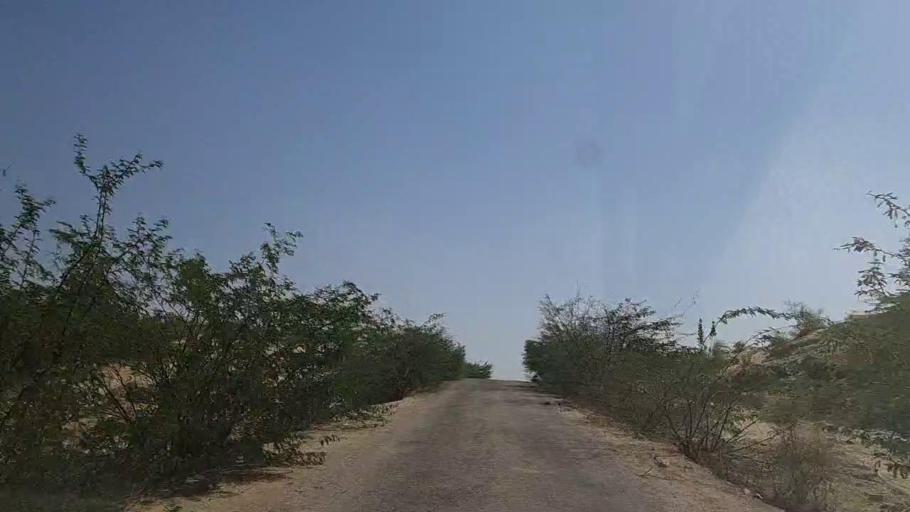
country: PK
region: Sindh
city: Diplo
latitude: 24.4872
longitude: 69.4458
